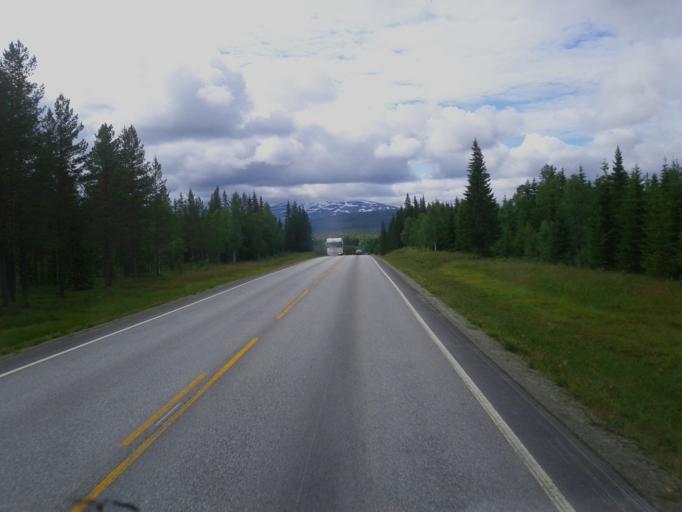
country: NO
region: Nord-Trondelag
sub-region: Namsskogan
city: Namsskogan
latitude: 64.7193
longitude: 12.8002
